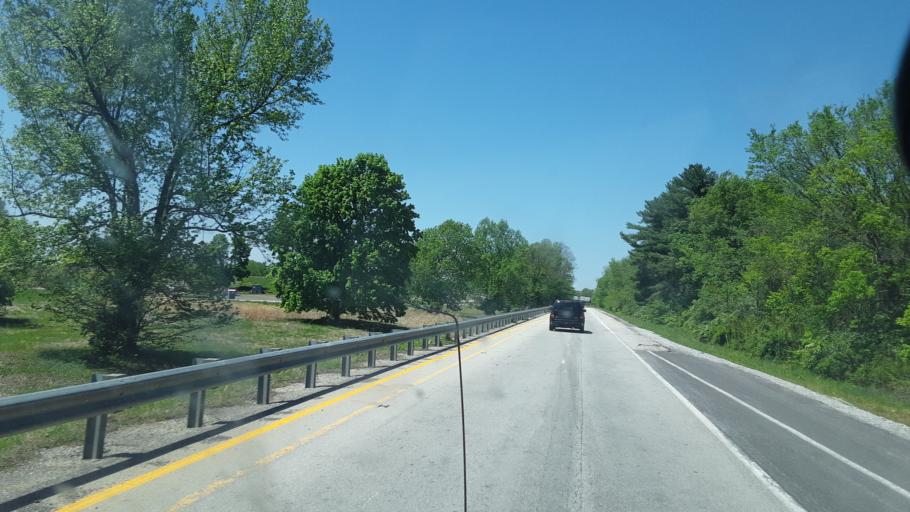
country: US
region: Kentucky
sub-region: Jefferson County
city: Worthington
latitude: 38.3170
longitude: -85.5796
